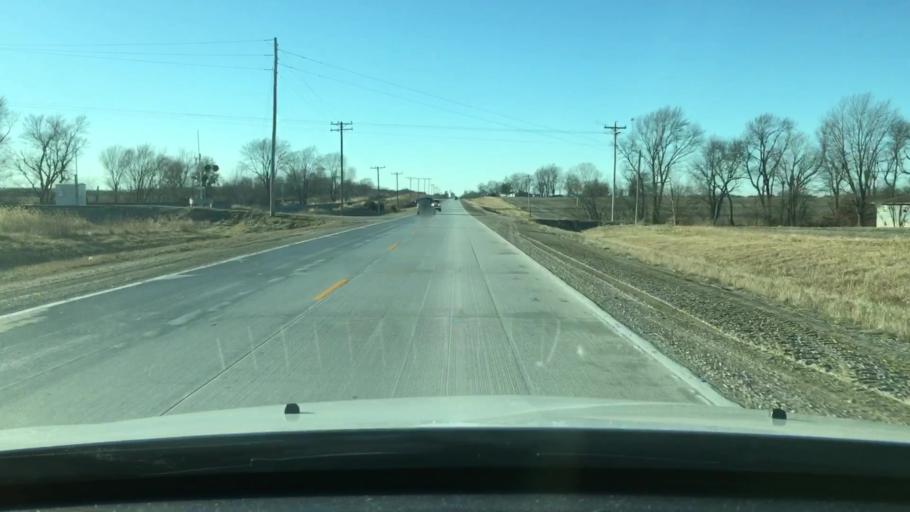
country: US
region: Missouri
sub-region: Boone County
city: Centralia
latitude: 39.2048
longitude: -92.0857
